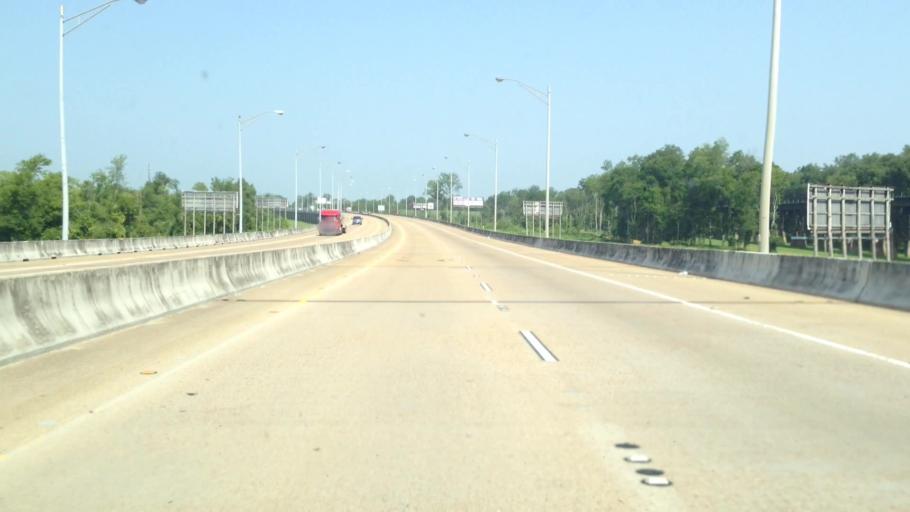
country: US
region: Mississippi
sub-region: Warren County
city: Vicksburg
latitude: 32.3181
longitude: -90.9142
